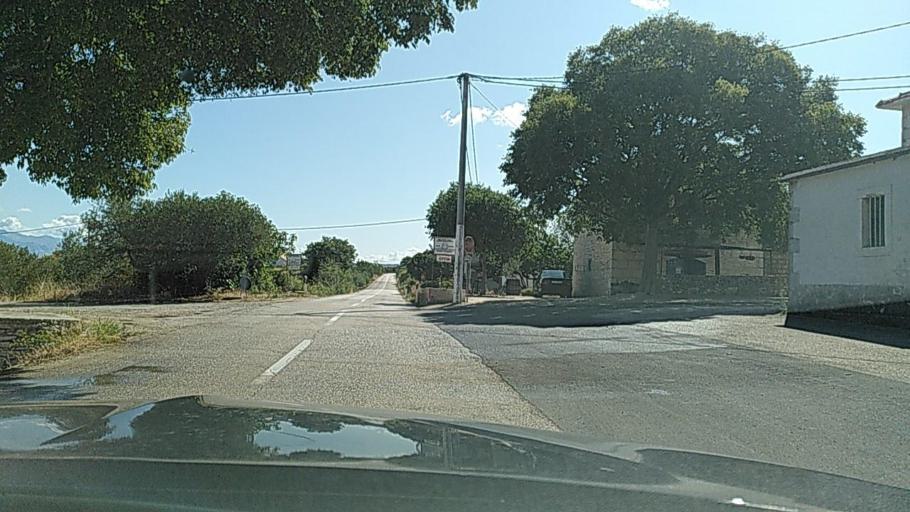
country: HR
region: Splitsko-Dalmatinska
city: Jelsa
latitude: 43.1490
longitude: 16.7936
